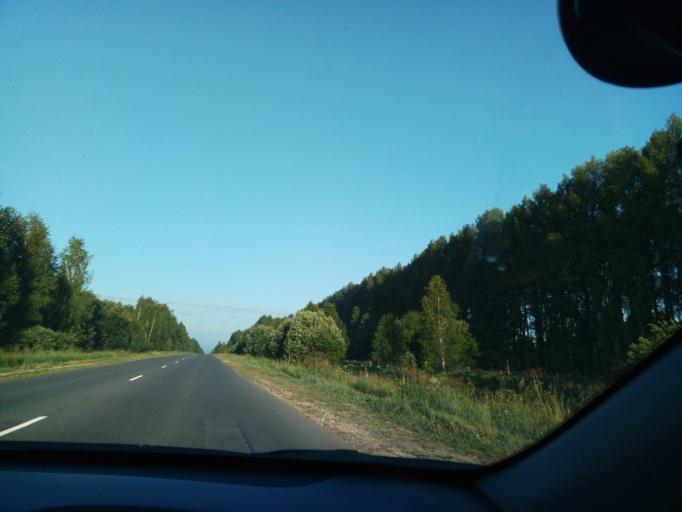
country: RU
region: Nizjnij Novgorod
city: Satis
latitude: 54.8997
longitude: 43.1303
